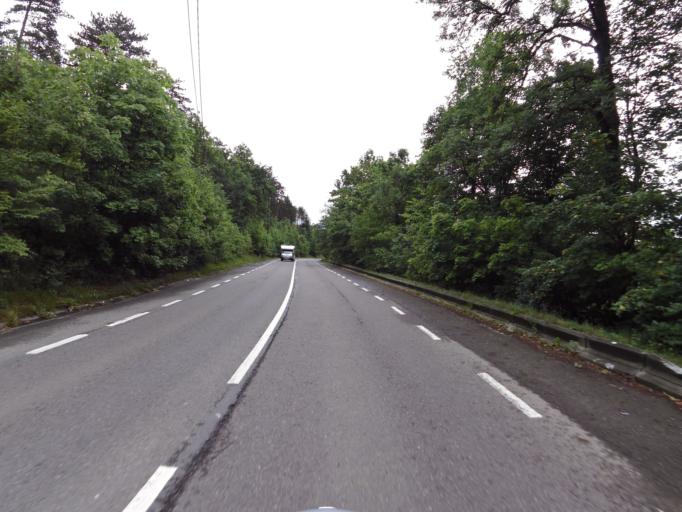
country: BE
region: Wallonia
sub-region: Province de Namur
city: Rochefort
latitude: 50.1353
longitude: 5.1847
